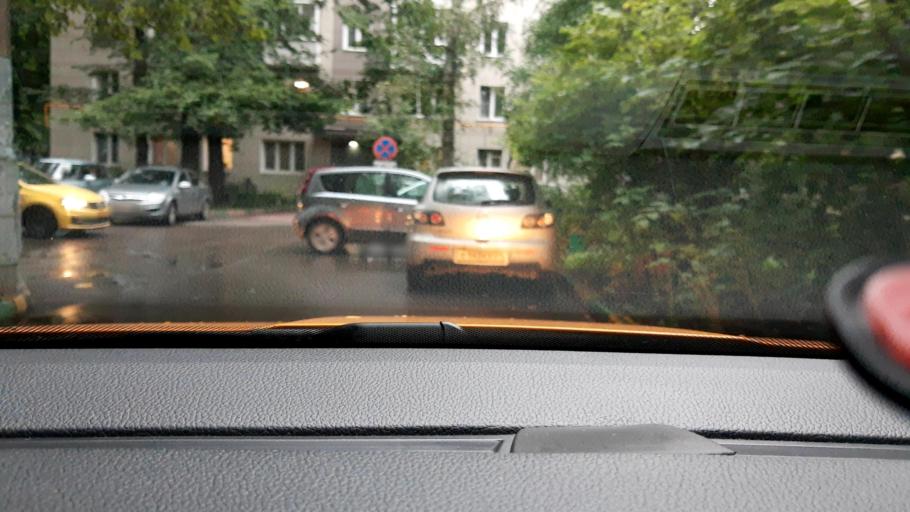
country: RU
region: Moskovskaya
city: Izmaylovo
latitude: 55.7891
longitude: 37.8038
